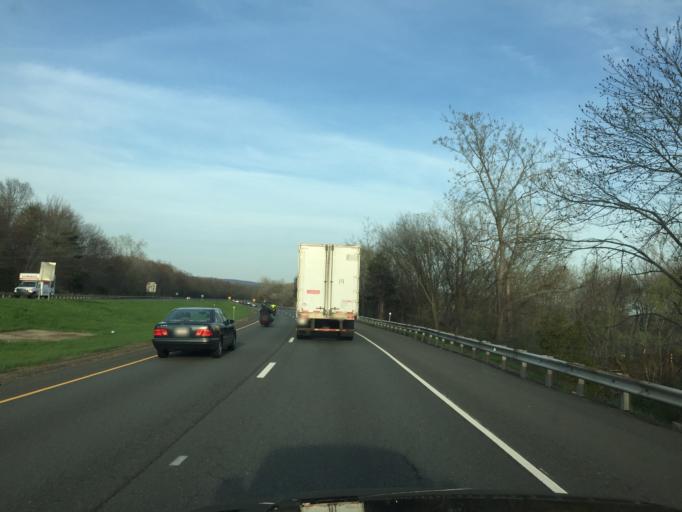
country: US
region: Connecticut
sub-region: Middlesex County
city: Cromwell
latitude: 41.5916
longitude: -72.6625
